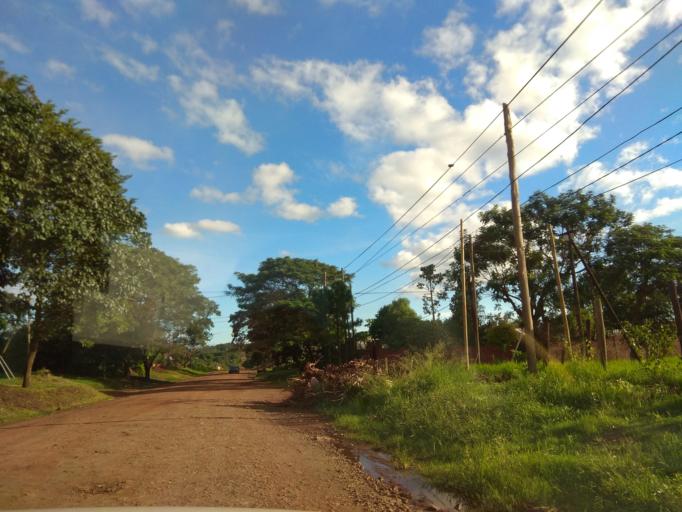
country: AR
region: Misiones
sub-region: Departamento de Capital
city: Posadas
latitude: -27.3902
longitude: -55.9273
